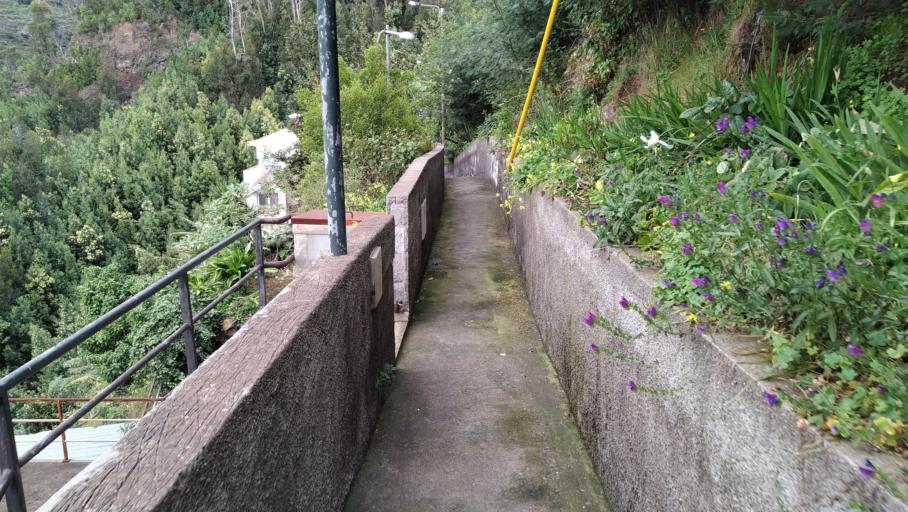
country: PT
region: Madeira
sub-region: Funchal
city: Nossa Senhora do Monte
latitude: 32.6674
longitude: -16.8928
